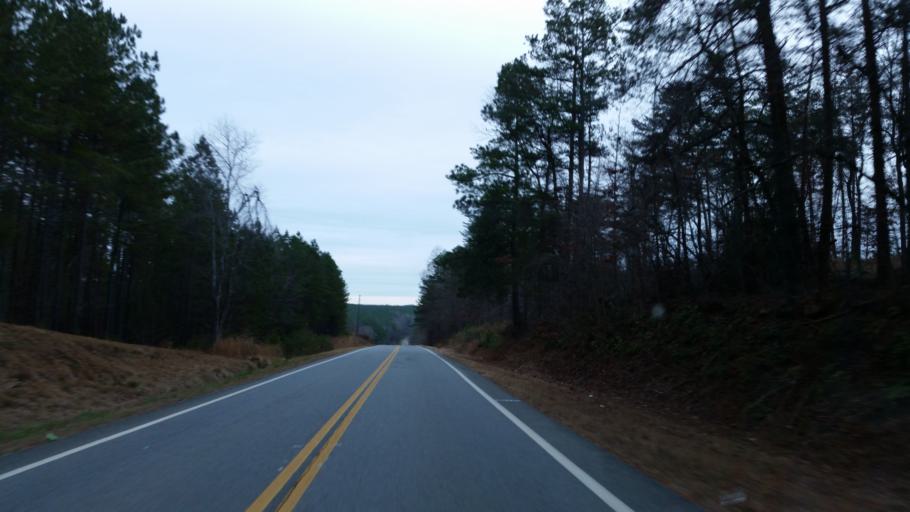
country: US
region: Georgia
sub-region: Dawson County
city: Dawsonville
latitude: 34.4529
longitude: -84.1328
